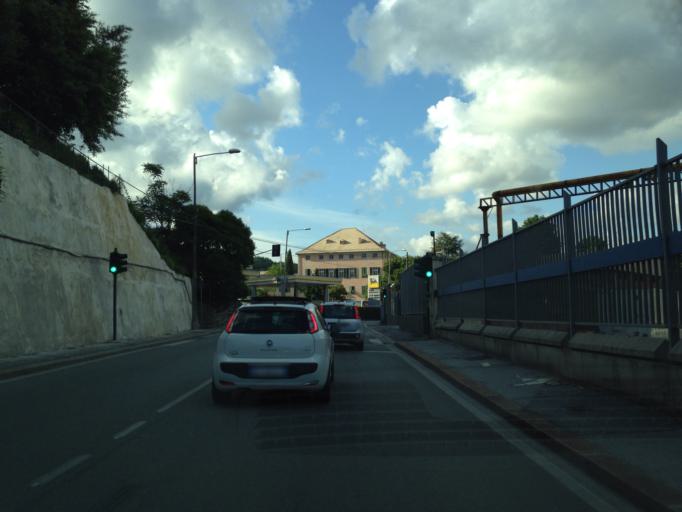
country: IT
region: Liguria
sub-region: Provincia di Genova
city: Genoa
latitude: 44.4340
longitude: 8.8859
